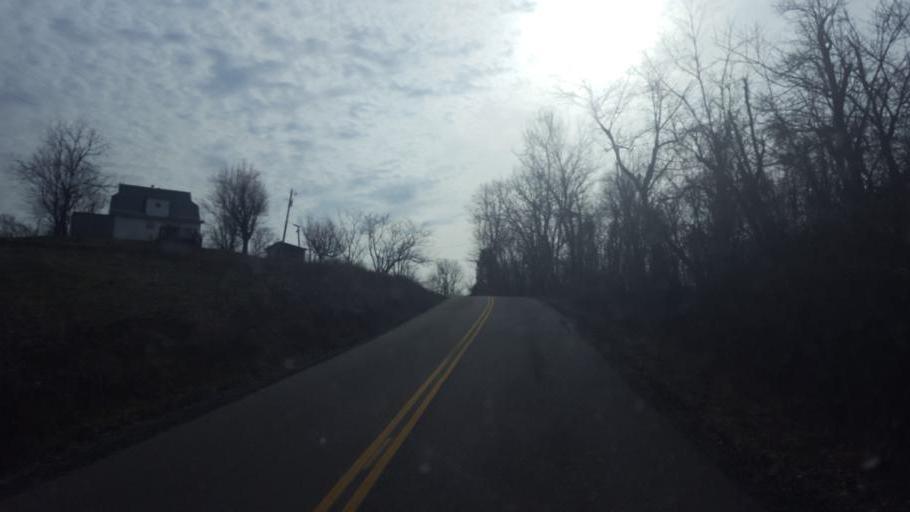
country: US
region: Ohio
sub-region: Gallia County
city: Gallipolis
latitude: 38.7117
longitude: -82.3415
